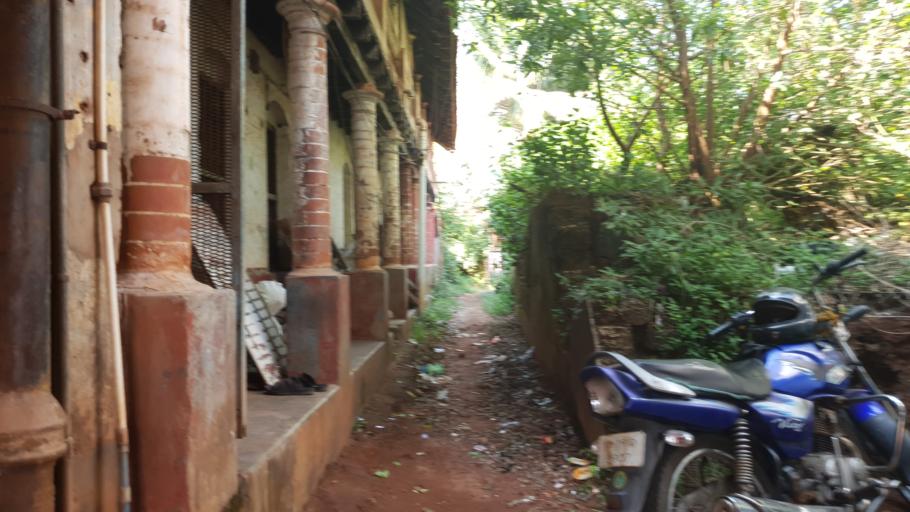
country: IN
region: Karnataka
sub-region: Dakshina Kannada
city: Mangalore
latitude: 12.8704
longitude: 74.8354
